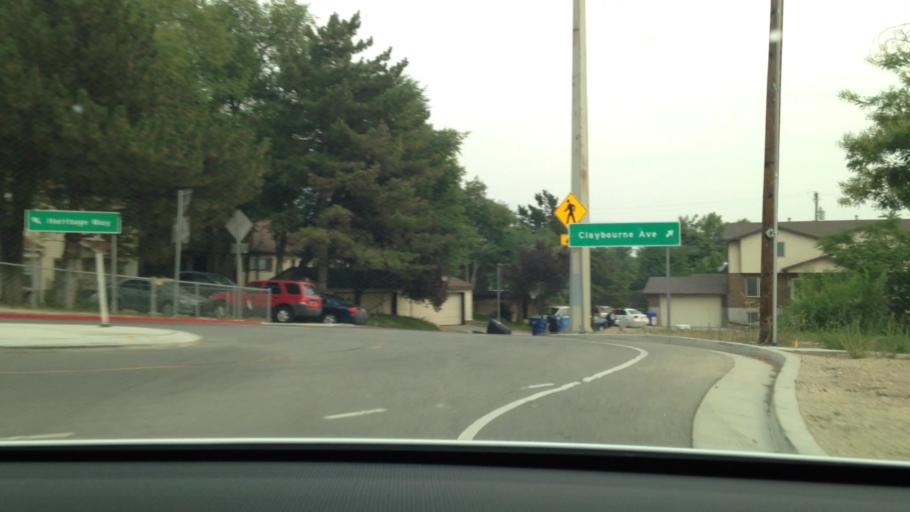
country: US
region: Utah
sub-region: Salt Lake County
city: Canyon Rim
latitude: 40.7114
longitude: -111.8233
